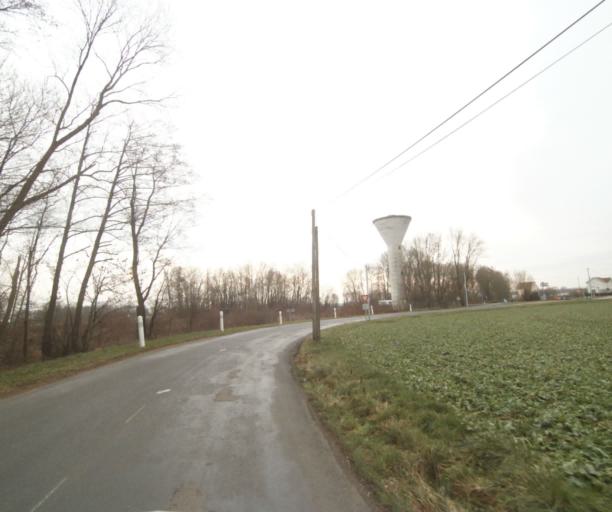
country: FR
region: Champagne-Ardenne
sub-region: Departement de la Haute-Marne
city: Villiers-en-Lieu
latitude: 48.6481
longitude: 4.8742
